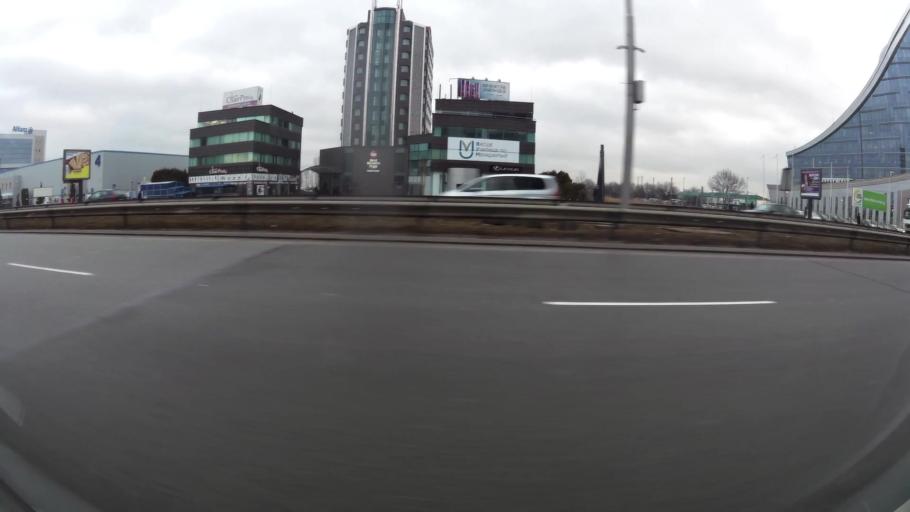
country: BG
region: Sofia-Capital
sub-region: Stolichna Obshtina
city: Sofia
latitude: 42.6474
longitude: 23.3964
